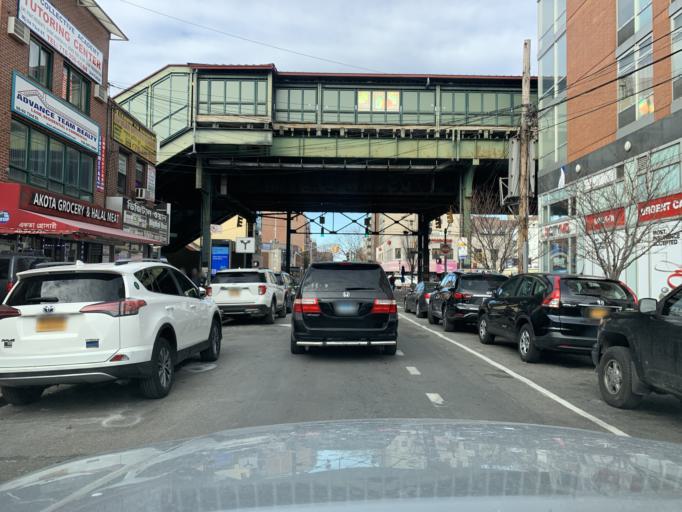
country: US
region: New York
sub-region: Queens County
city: Long Island City
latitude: 40.7464
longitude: -73.8922
